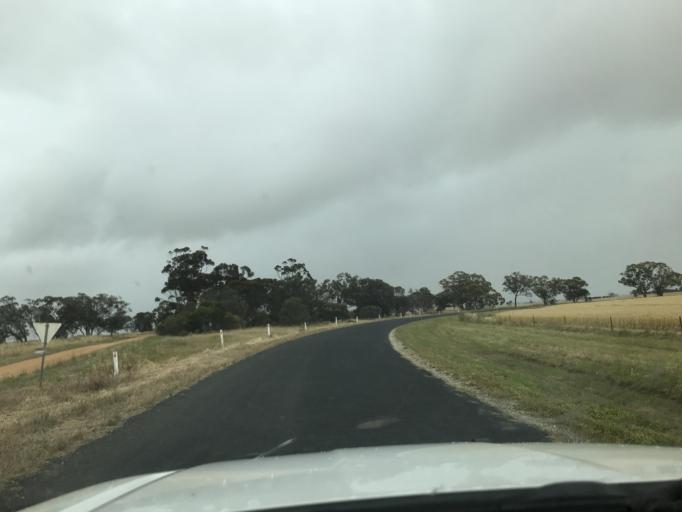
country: AU
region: South Australia
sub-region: Tatiara
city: Bordertown
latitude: -36.3428
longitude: 141.2171
